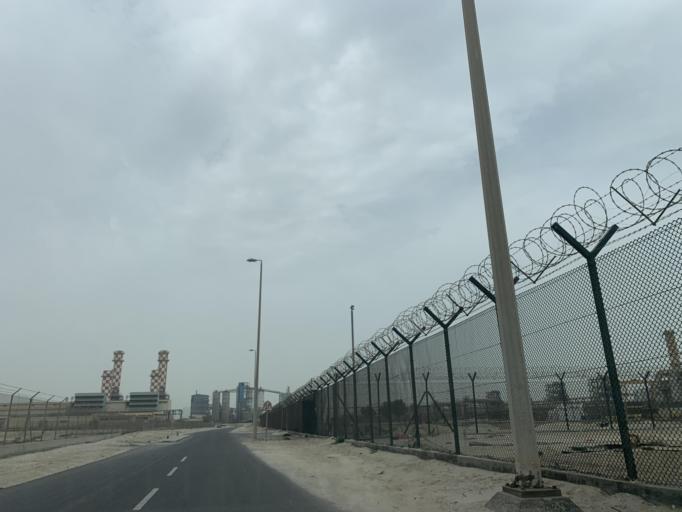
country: BH
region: Muharraq
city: Al Hadd
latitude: 26.2192
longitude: 50.6641
